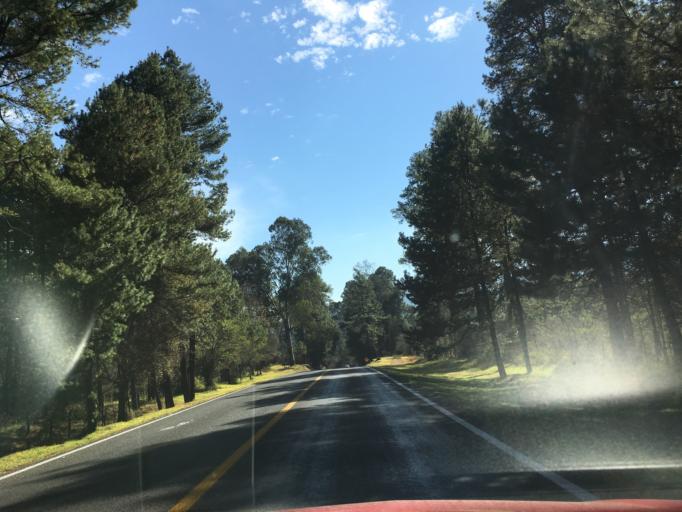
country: MX
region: Michoacan
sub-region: Hidalgo
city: Tierras Coloradas (San Pedro)
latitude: 19.6688
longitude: -100.6887
